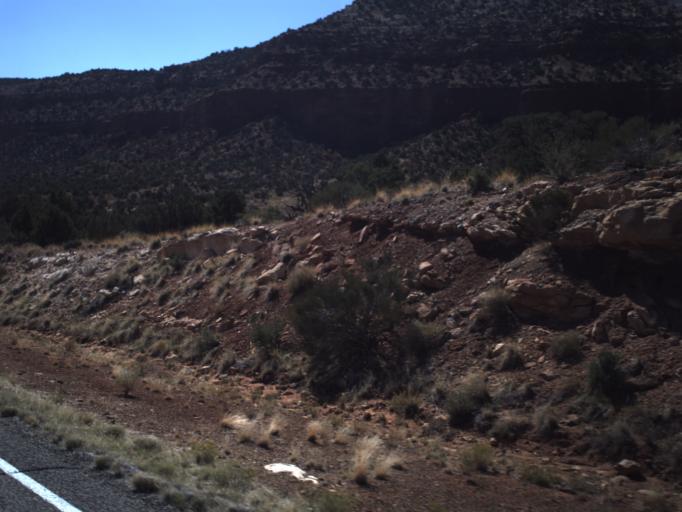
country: US
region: Utah
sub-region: San Juan County
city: Blanding
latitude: 37.6442
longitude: -110.1124
